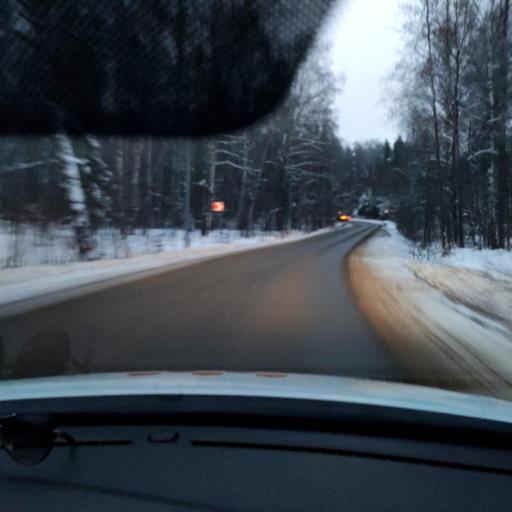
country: RU
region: Tatarstan
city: Vysokaya Gora
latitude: 55.9305
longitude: 49.1574
